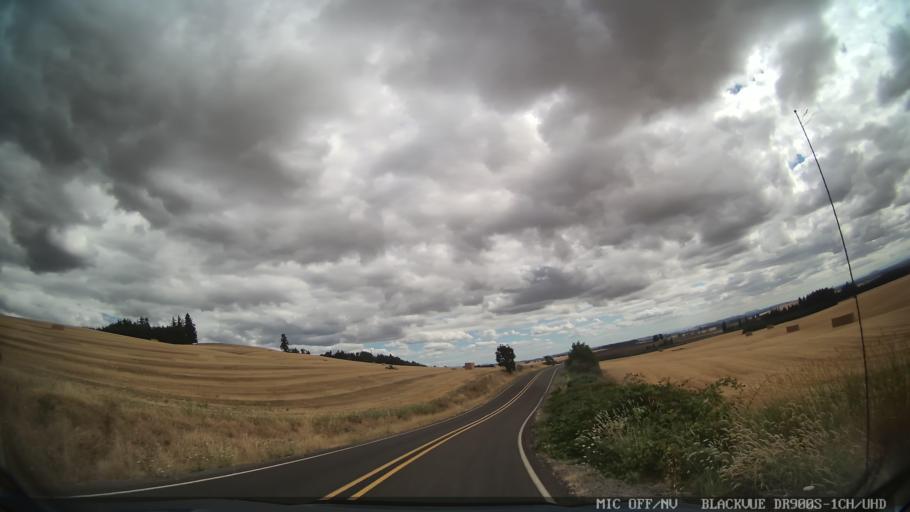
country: US
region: Oregon
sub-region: Marion County
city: Sublimity
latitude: 44.8677
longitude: -122.7395
